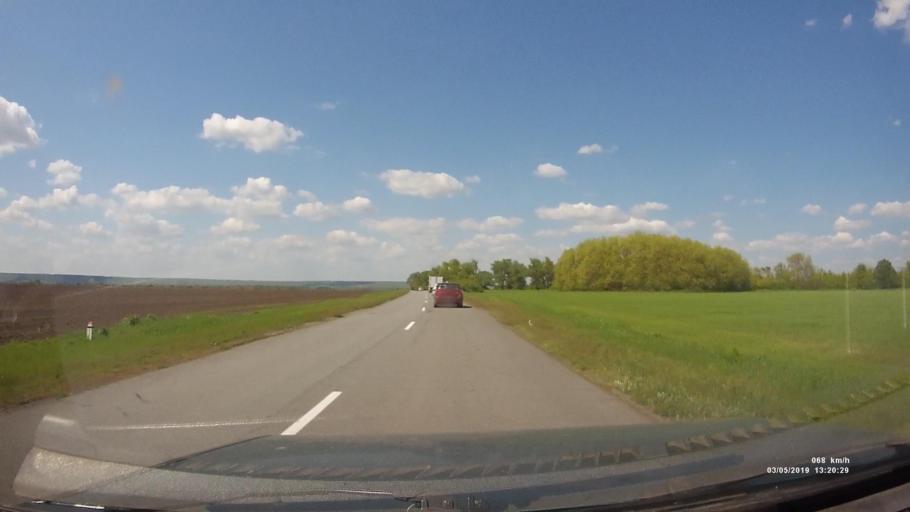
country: RU
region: Rostov
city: Semikarakorsk
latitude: 47.5467
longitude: 40.7532
